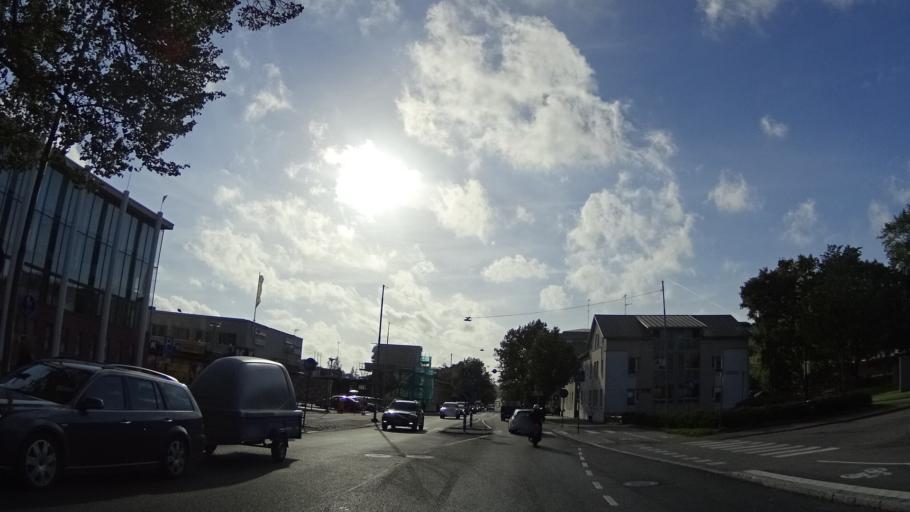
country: FI
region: Uusimaa
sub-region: Porvoo
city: Porvoo
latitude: 60.3960
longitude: 25.6689
